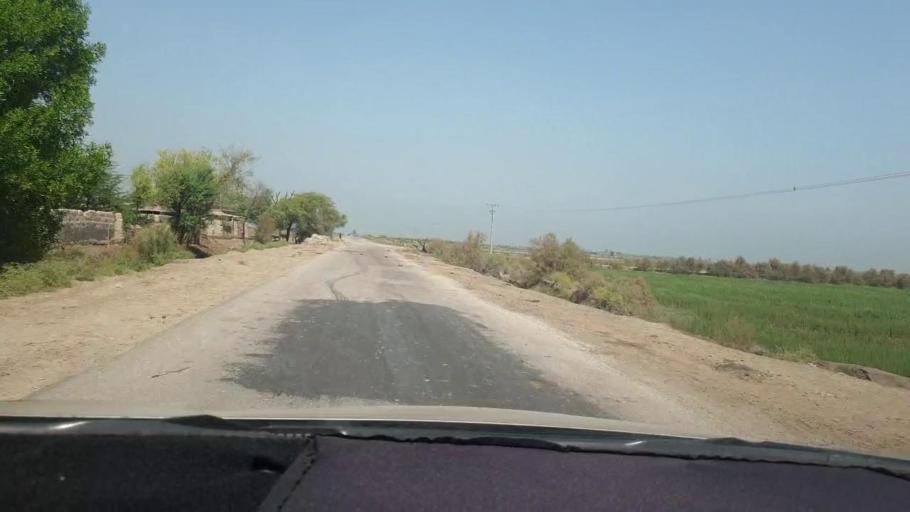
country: PK
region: Sindh
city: Miro Khan
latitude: 27.8277
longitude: 68.0176
